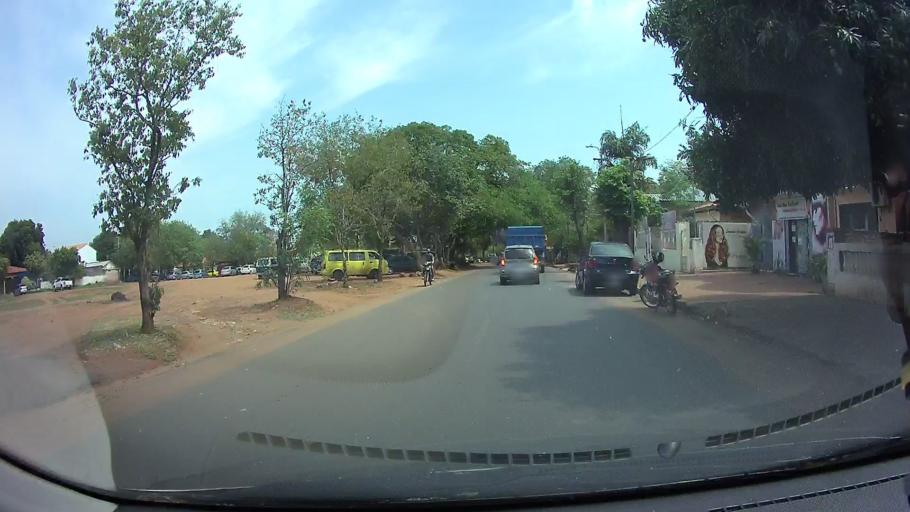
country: PY
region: Central
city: Itaugua
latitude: -25.3910
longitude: -57.3549
